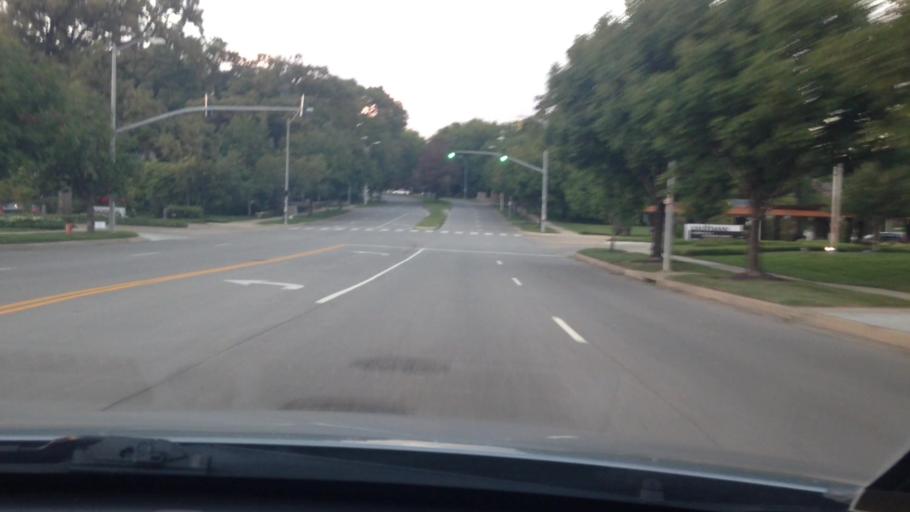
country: US
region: Kansas
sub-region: Johnson County
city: Westwood
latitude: 39.0394
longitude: -94.5785
